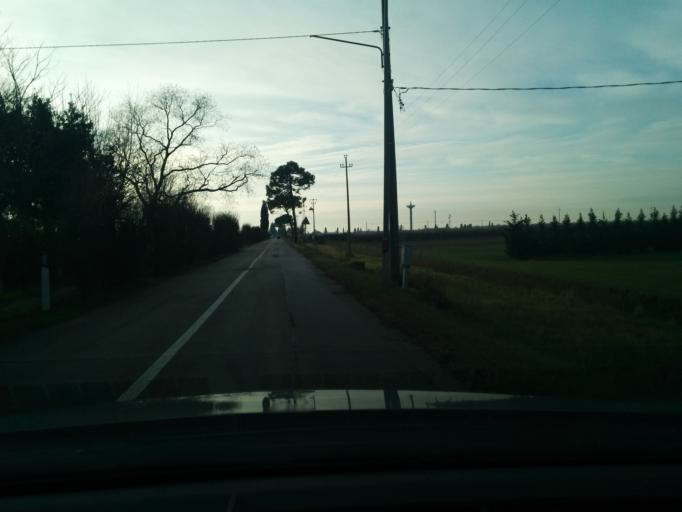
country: IT
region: Friuli Venezia Giulia
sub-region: Provincia di Gorizia
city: San Canzian d'Isonzo
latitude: 45.7204
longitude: 13.4735
